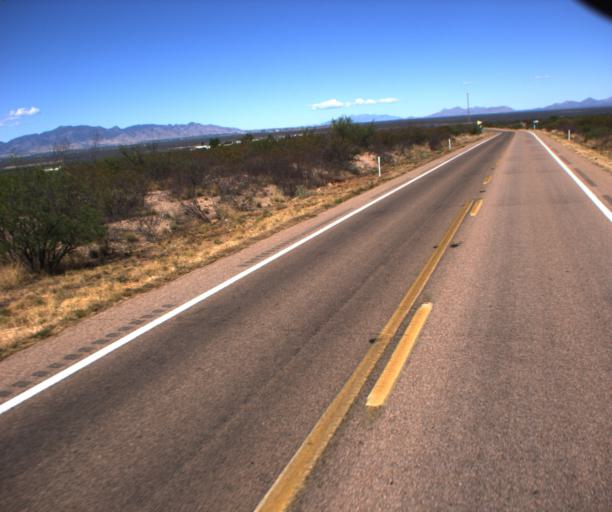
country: US
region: Arizona
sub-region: Cochise County
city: Sierra Vista Southeast
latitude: 31.5464
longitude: -110.0978
